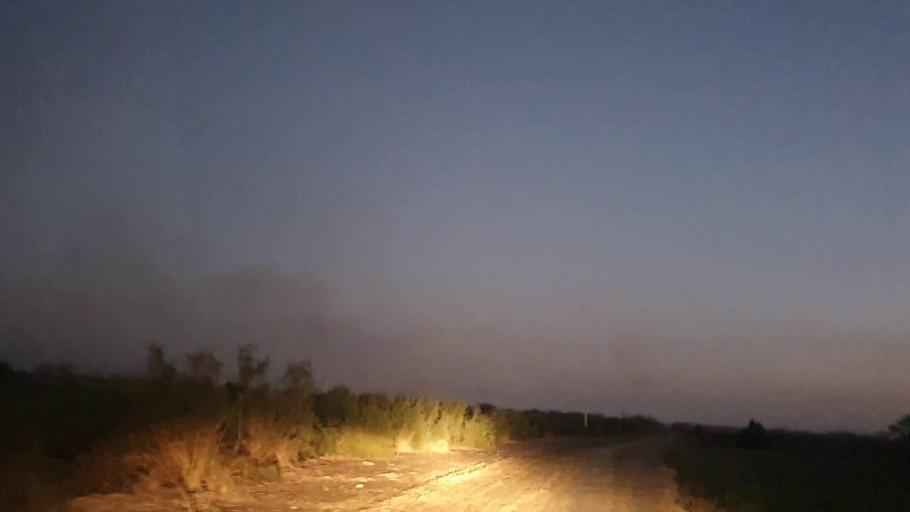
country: PK
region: Sindh
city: Nawabshah
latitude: 26.3246
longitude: 68.3777
